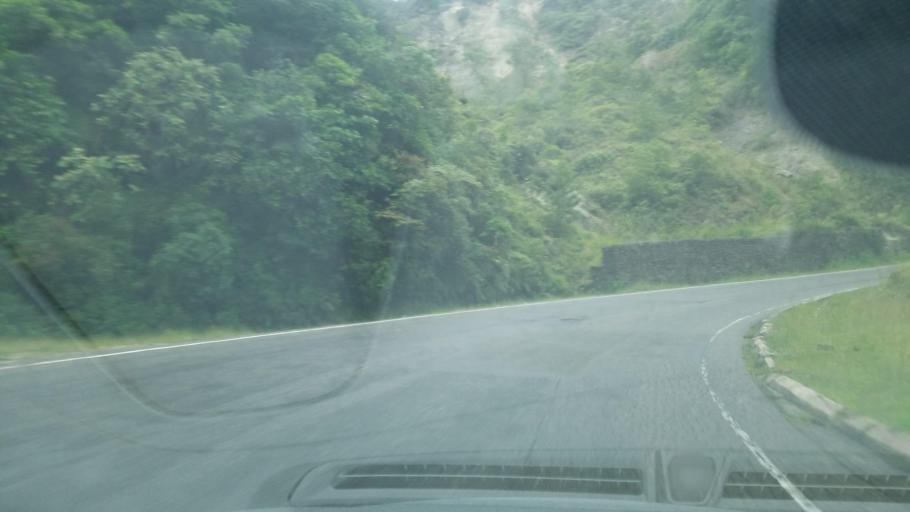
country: HN
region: Ocotepeque
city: La Labor
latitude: 14.4665
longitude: -89.0676
